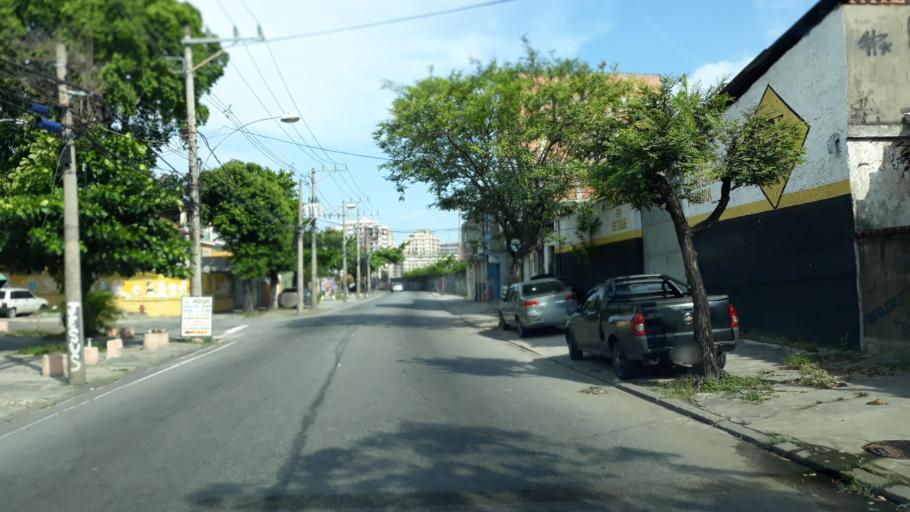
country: BR
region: Rio de Janeiro
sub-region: Duque De Caxias
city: Duque de Caxias
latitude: -22.8417
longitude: -43.2730
